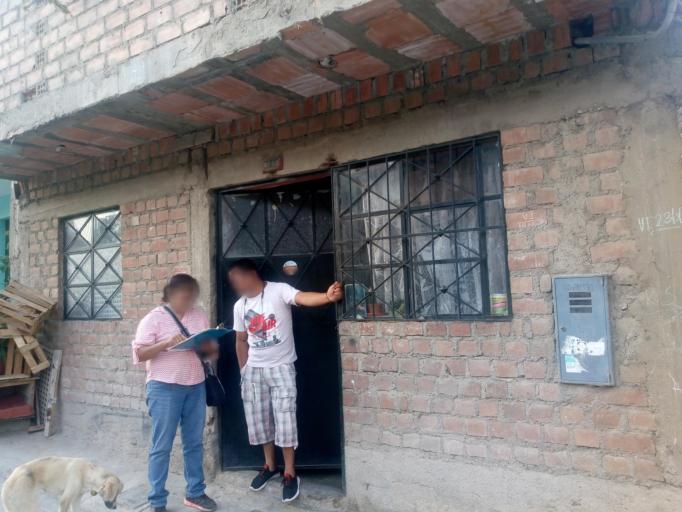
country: PE
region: Lima
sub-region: Provincia de Huarochiri
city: Ricardo Palma
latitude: -11.9224
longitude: -76.6682
